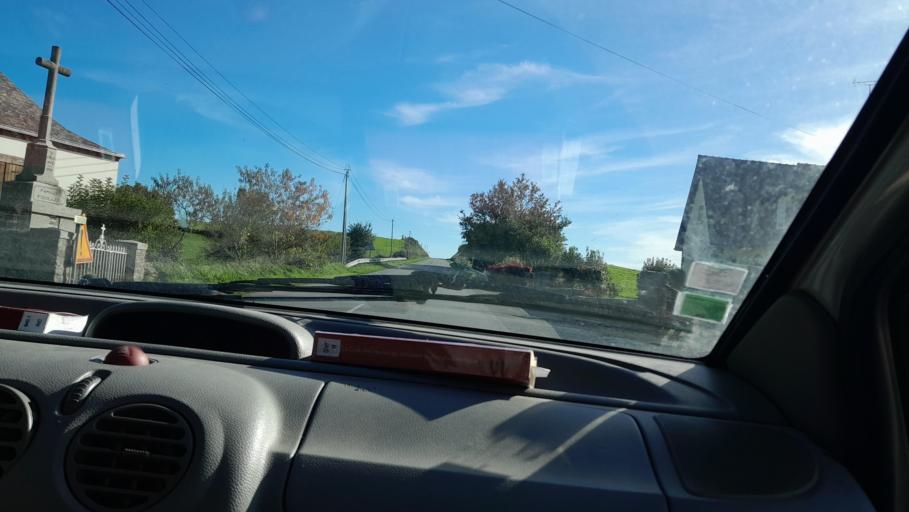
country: FR
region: Brittany
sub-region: Departement d'Ille-et-Vilaine
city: Argentre-du-Plessis
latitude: 47.9859
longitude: -1.1233
